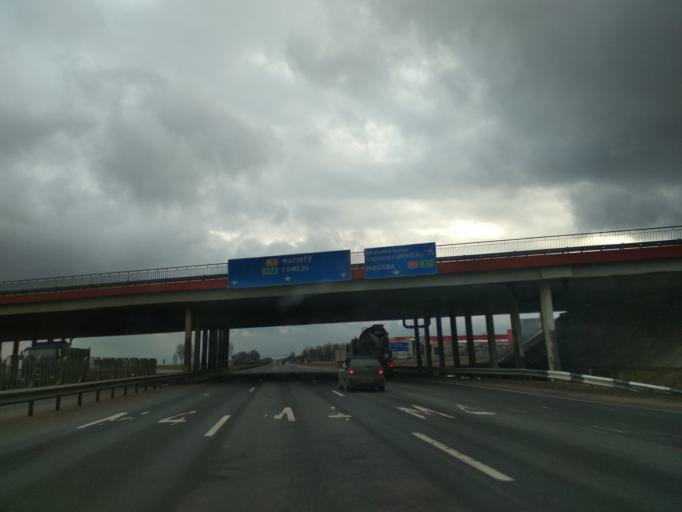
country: BY
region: Minsk
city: Pryvol'ny
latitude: 53.8050
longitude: 27.7931
